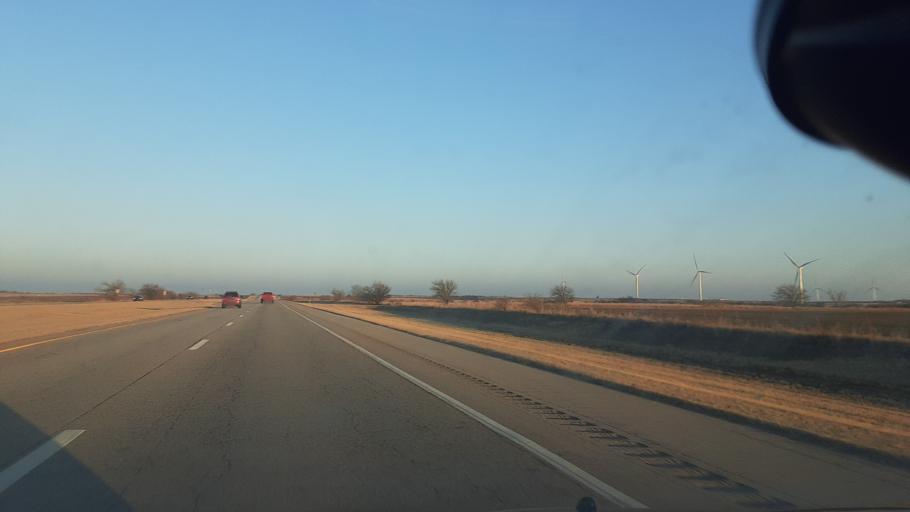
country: US
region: Oklahoma
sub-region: Noble County
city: Perry
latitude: 36.3979
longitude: -97.4014
